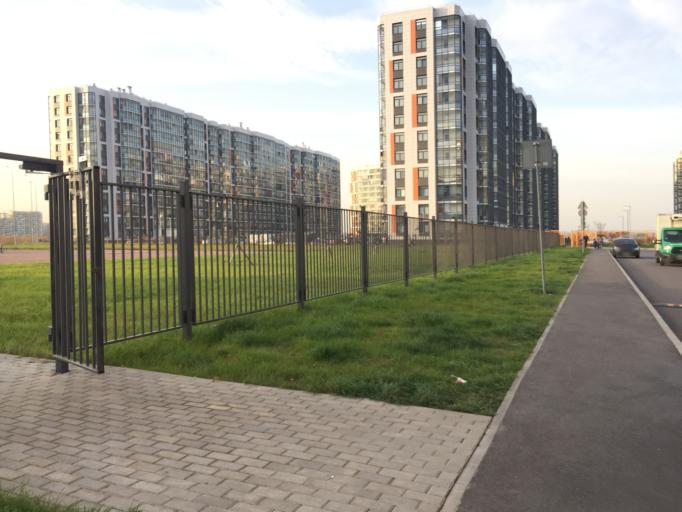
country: RU
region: St.-Petersburg
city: Grazhdanka
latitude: 60.0567
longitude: 30.4170
